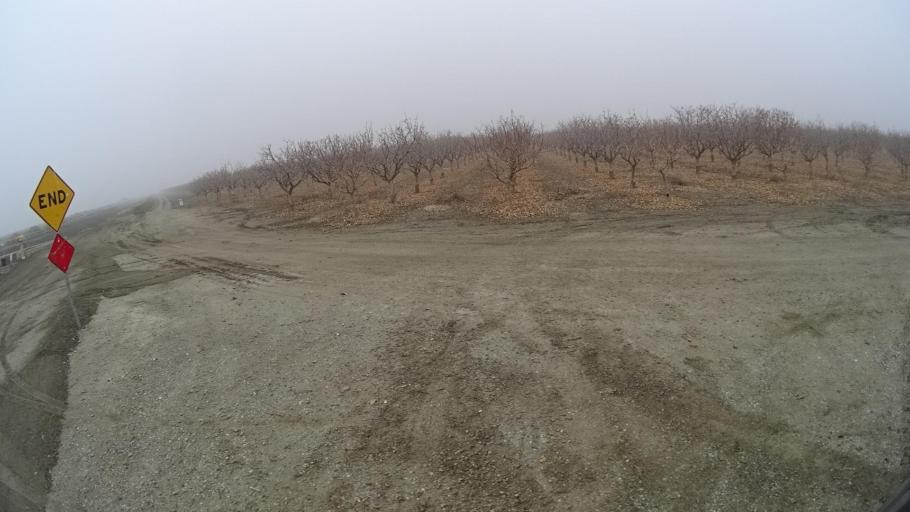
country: US
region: California
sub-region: Kern County
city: Buttonwillow
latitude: 35.4123
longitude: -119.5485
